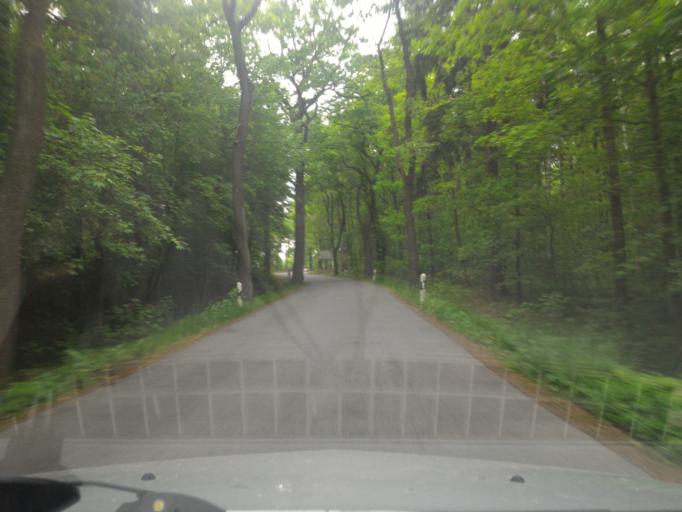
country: DE
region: Saxony
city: Bertsdorf-Hoernitz
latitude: 50.8681
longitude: 14.7496
